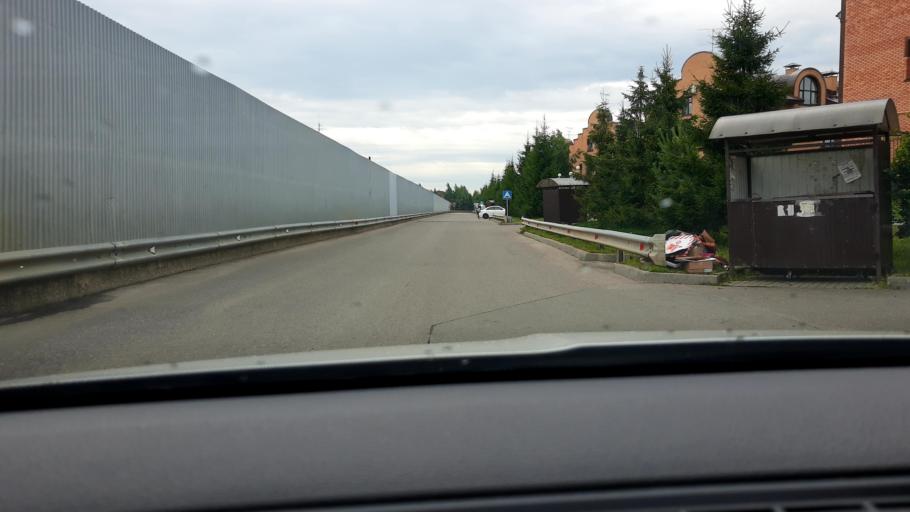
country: RU
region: Moskovskaya
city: Troitsk
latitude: 55.4937
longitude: 37.2593
